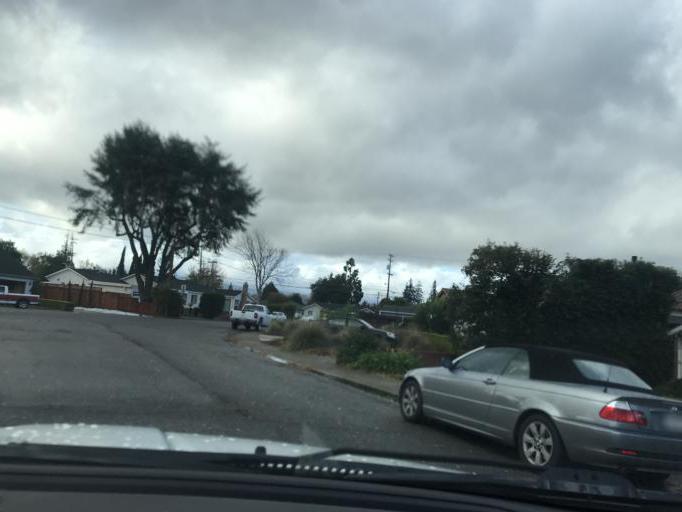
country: US
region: California
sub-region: Santa Clara County
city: Buena Vista
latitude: 37.3000
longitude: -121.9125
